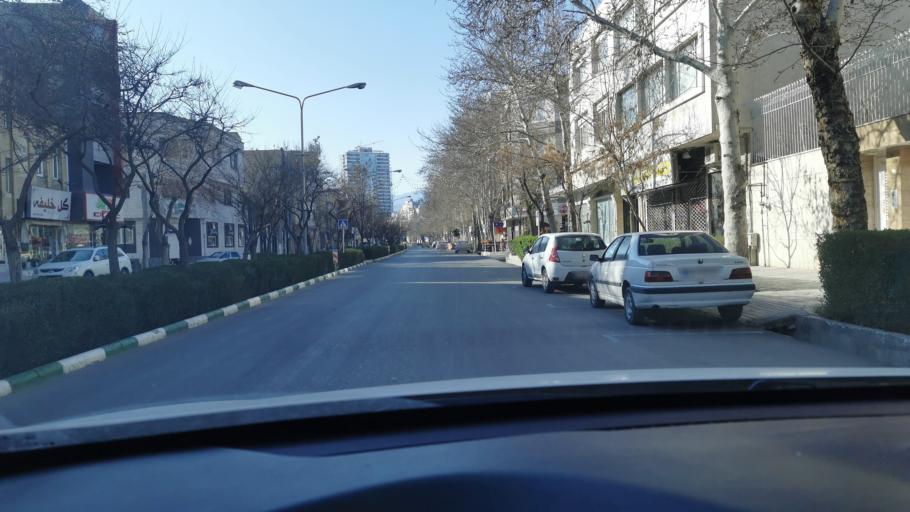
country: IR
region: Razavi Khorasan
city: Mashhad
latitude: 36.2904
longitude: 59.5674
